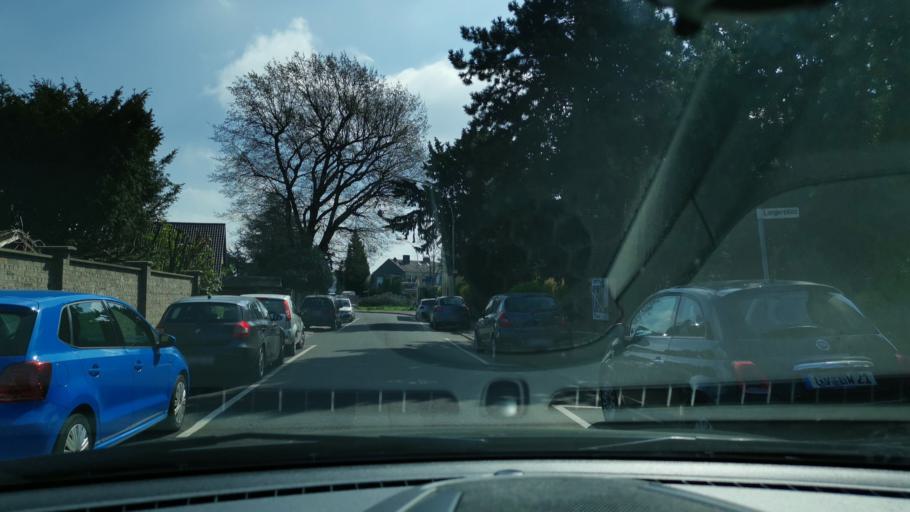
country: DE
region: North Rhine-Westphalia
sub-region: Regierungsbezirk Dusseldorf
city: Grevenbroich
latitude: 51.0851
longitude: 6.5999
